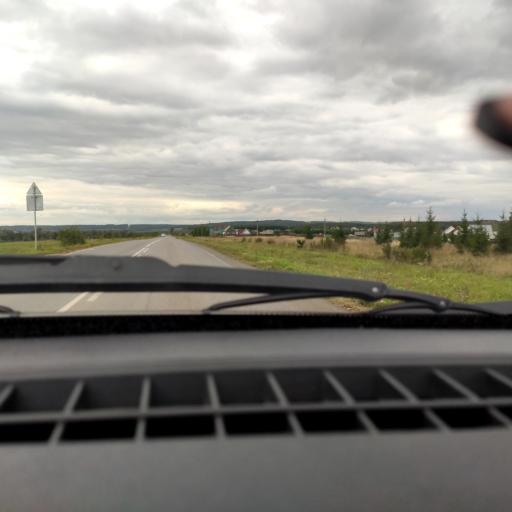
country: RU
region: Bashkortostan
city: Iglino
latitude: 54.7101
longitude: 56.4001
